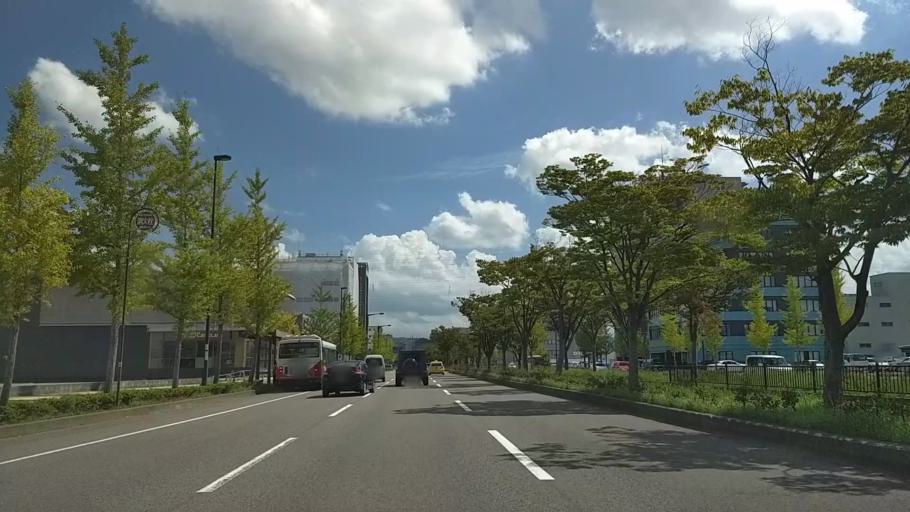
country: JP
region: Ishikawa
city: Kanazawa-shi
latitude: 36.5878
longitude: 136.6350
